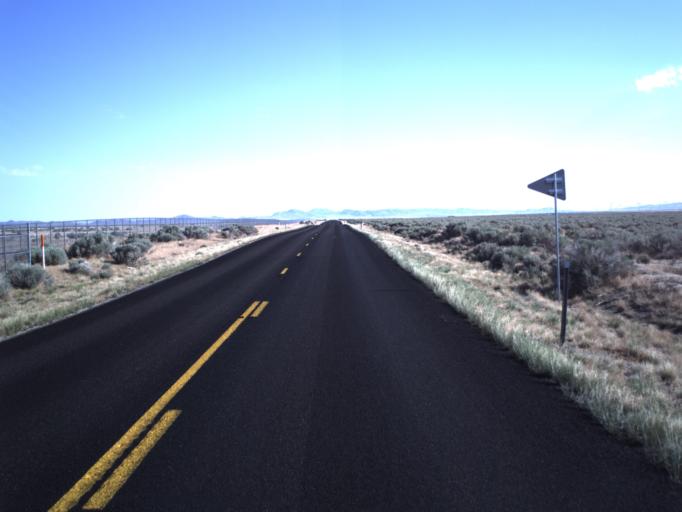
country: US
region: Utah
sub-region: Beaver County
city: Milford
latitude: 38.4214
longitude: -113.0099
